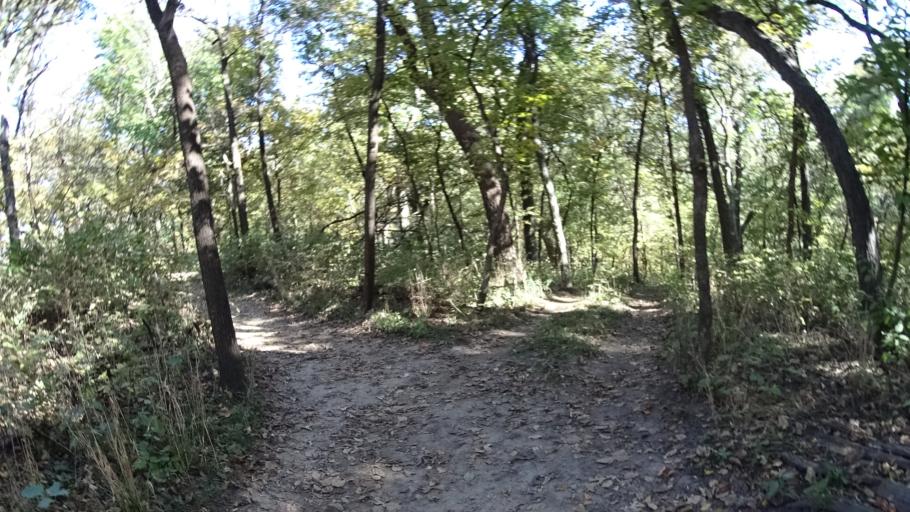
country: US
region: Nebraska
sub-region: Sarpy County
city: Bellevue
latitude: 41.1804
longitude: -95.9149
